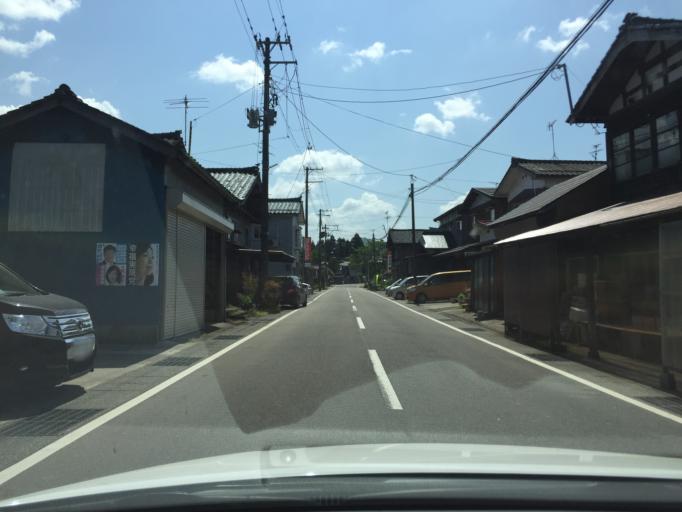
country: JP
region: Niigata
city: Tochio-honcho
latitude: 37.5477
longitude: 139.0883
